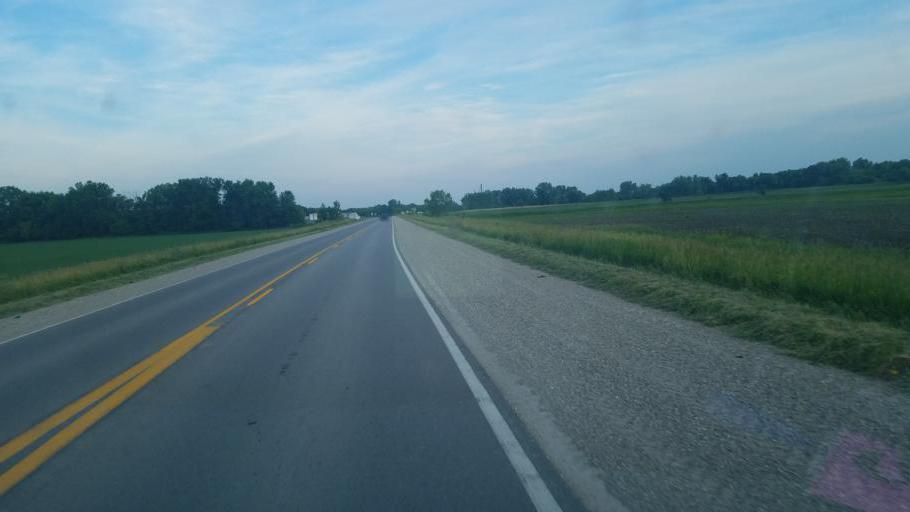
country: US
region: Iowa
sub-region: Benton County
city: Belle Plaine
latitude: 41.9049
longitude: -92.2953
